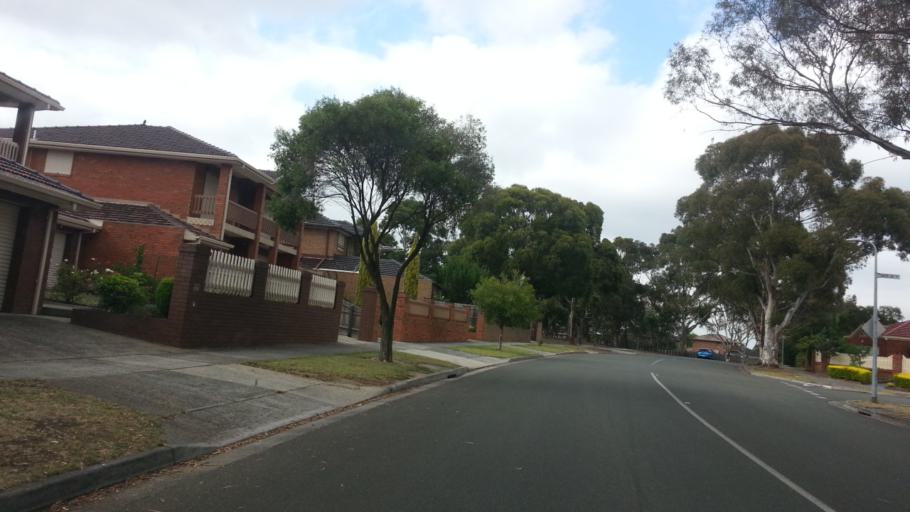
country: AU
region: Victoria
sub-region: Knox
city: Rowville
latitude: -37.9236
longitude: 145.2436
